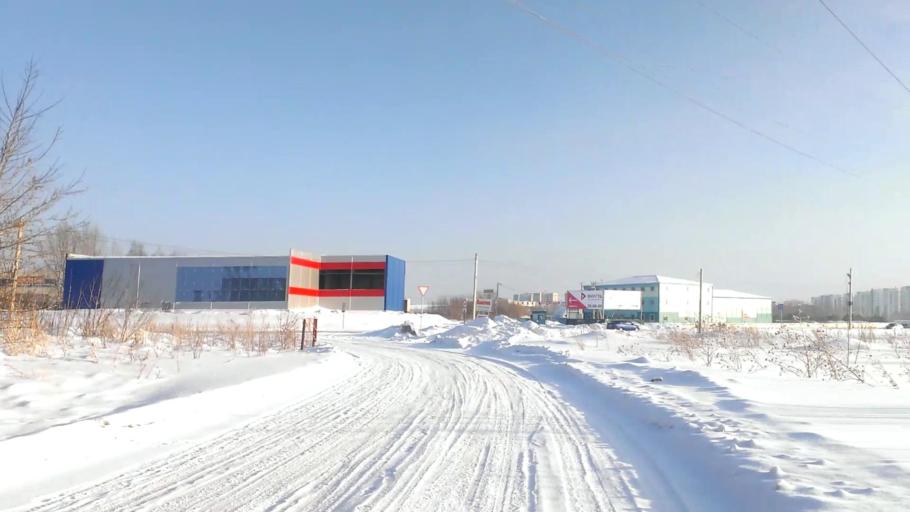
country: RU
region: Altai Krai
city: Novosilikatnyy
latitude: 53.3468
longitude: 83.6307
